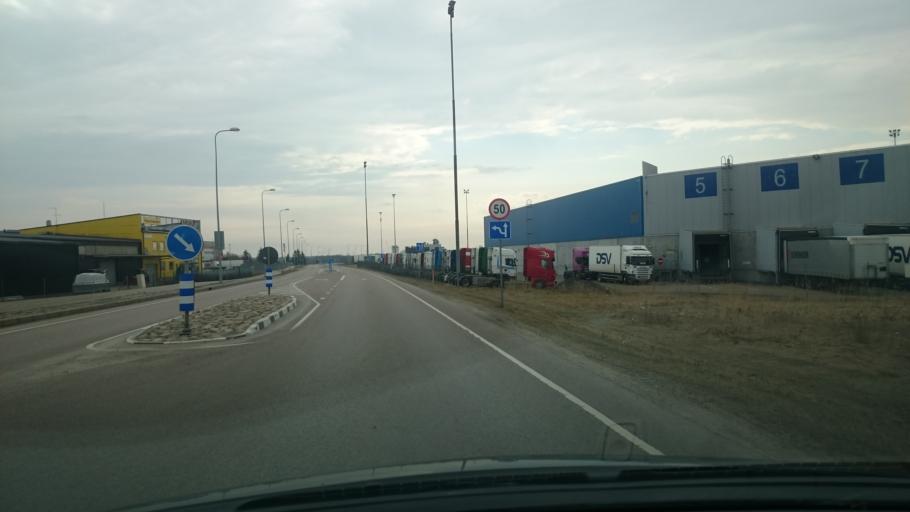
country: EE
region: Harju
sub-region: Saue vald
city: Laagri
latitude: 59.3416
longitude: 24.6213
